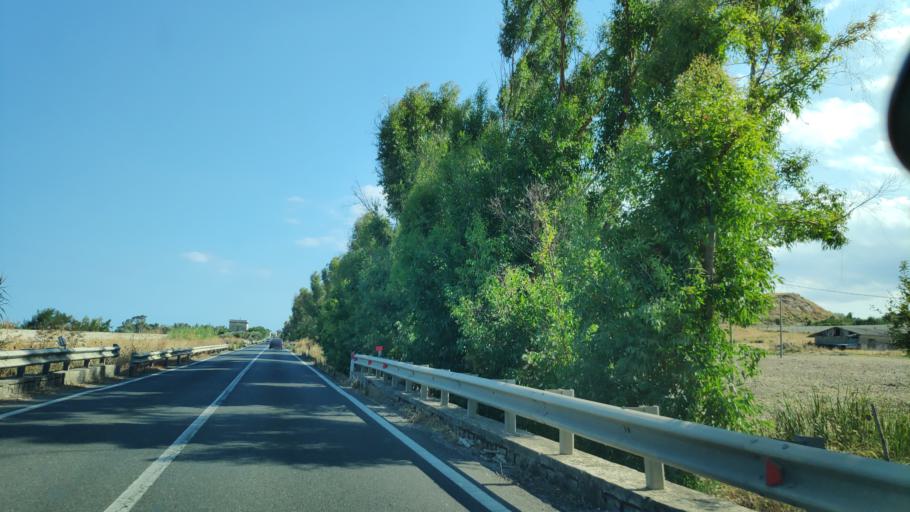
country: IT
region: Calabria
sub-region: Provincia di Catanzaro
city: Santa Caterina dello Ionio Marina
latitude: 38.5101
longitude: 16.5744
